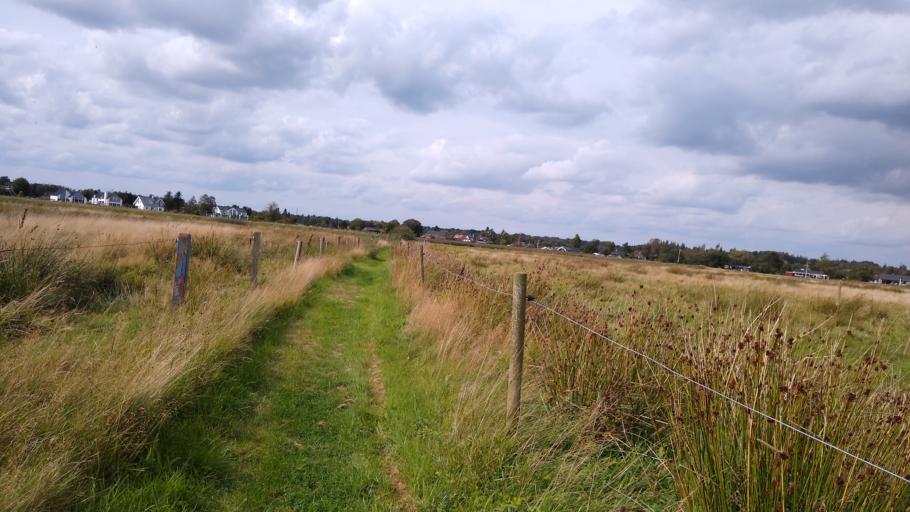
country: DK
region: South Denmark
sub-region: Fredericia Kommune
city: Fredericia
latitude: 55.6260
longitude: 9.7451
